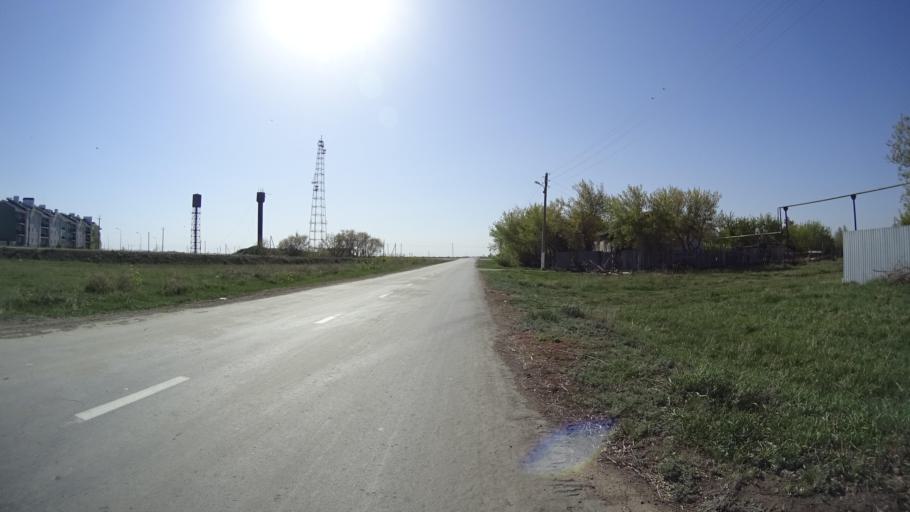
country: RU
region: Chelyabinsk
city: Chesma
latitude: 53.7915
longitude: 61.0392
